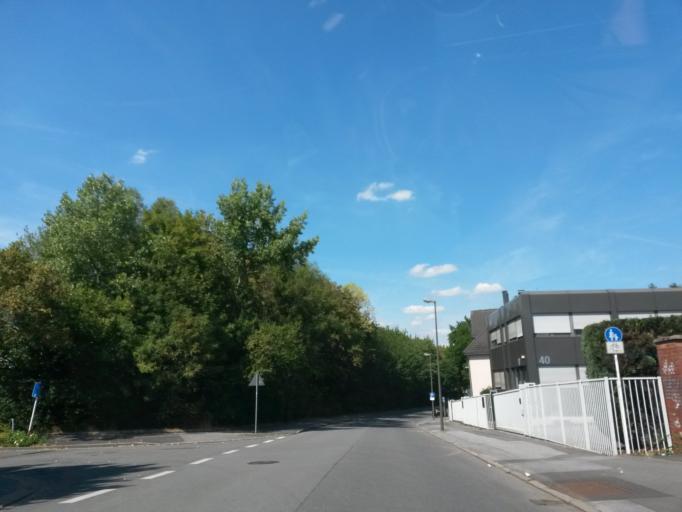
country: DE
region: North Rhine-Westphalia
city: Witten
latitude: 51.4914
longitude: 7.3647
